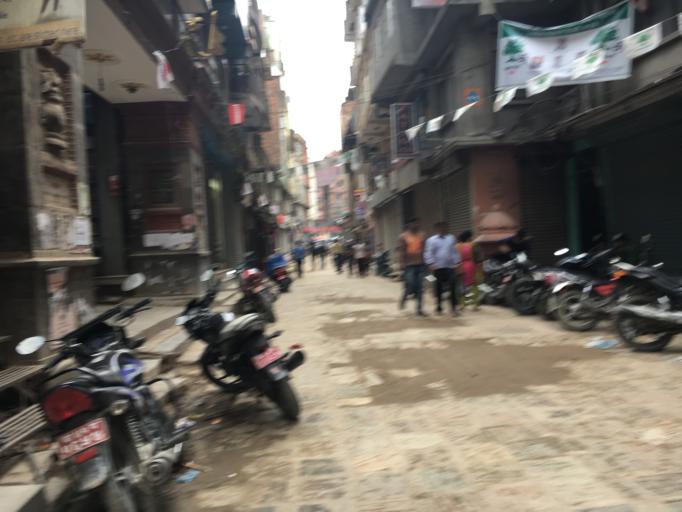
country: NP
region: Central Region
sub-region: Bagmati Zone
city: Kathmandu
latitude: 27.7094
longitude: 85.3106
